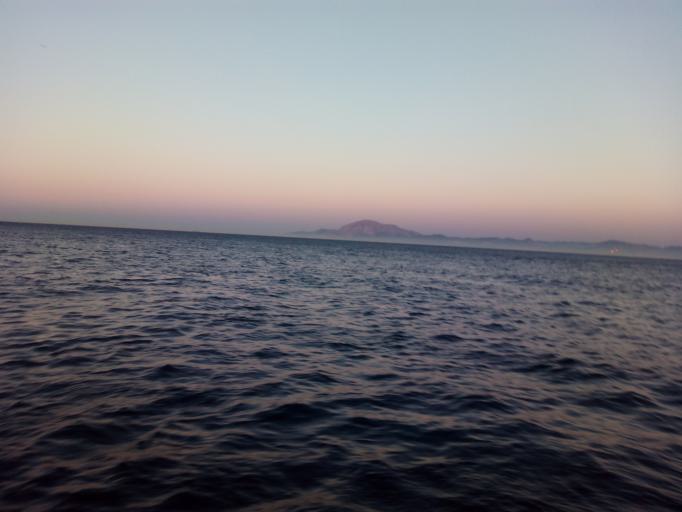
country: ES
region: Andalusia
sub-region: Provincia de Cadiz
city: Tarifa
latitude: 36.0044
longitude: -5.6054
